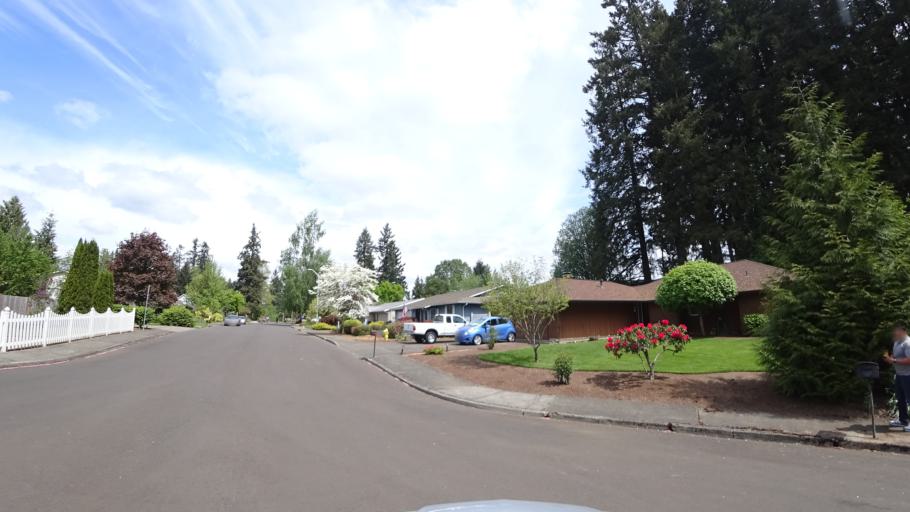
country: US
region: Oregon
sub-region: Washington County
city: Hillsboro
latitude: 45.5376
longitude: -122.9900
